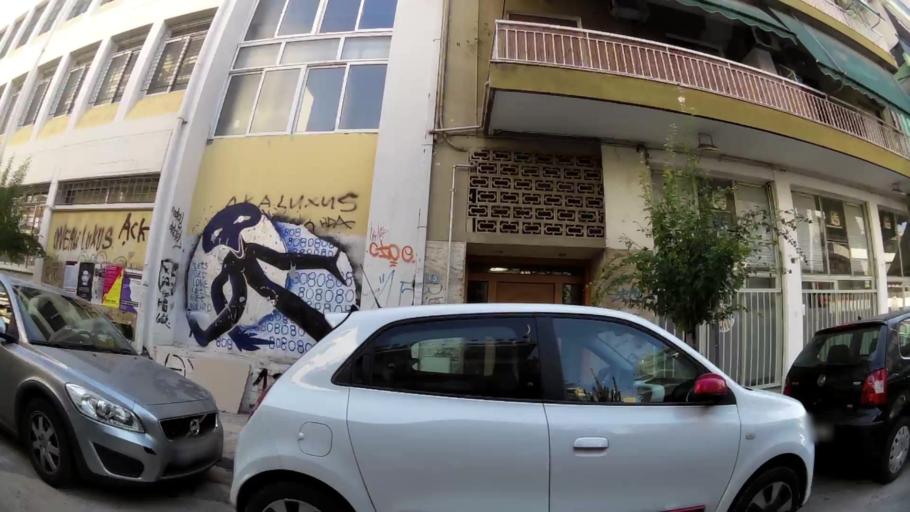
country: GR
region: Attica
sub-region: Nomarchia Athinas
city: Athens
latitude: 37.9737
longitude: 23.7108
